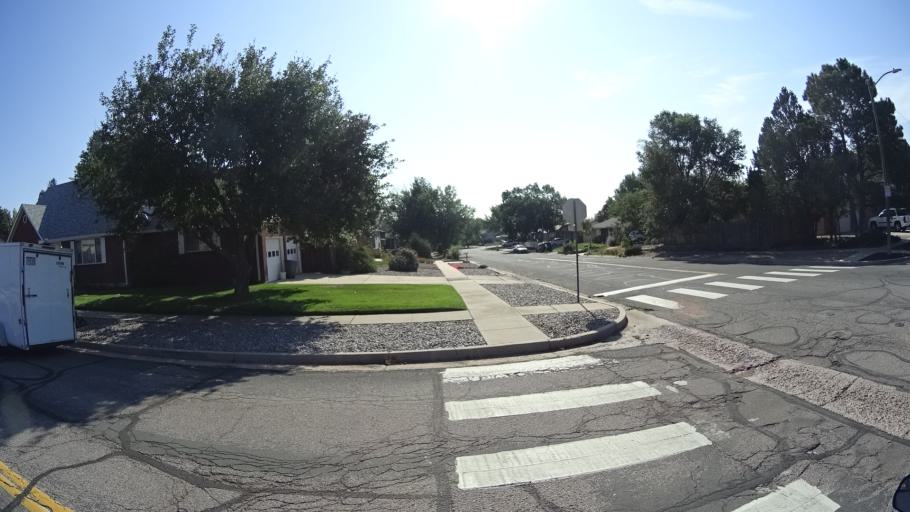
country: US
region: Colorado
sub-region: El Paso County
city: Colorado Springs
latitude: 38.8909
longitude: -104.8389
